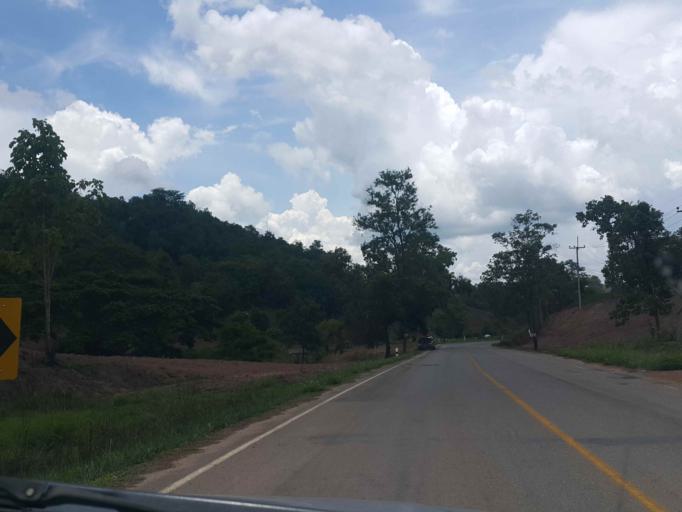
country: TH
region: Phayao
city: Chiang Muan
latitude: 18.9005
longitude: 100.1317
